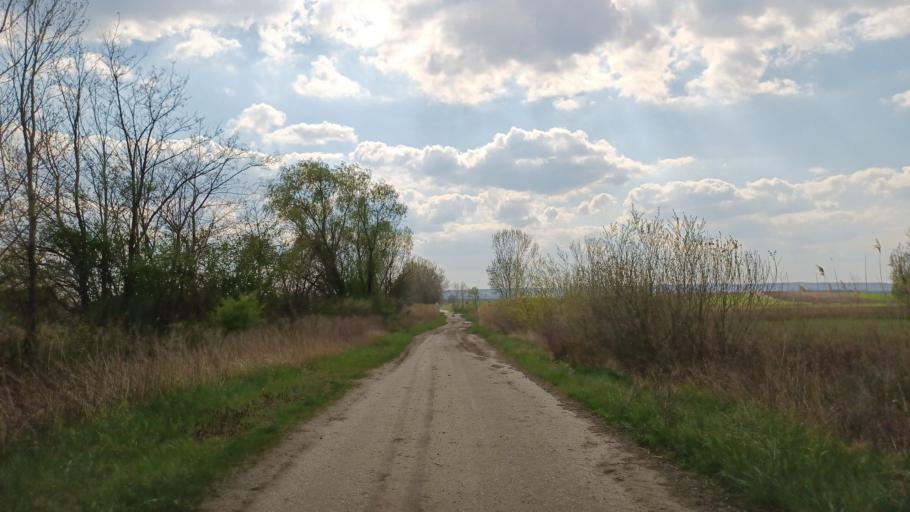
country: HU
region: Fejer
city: Cece
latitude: 46.7420
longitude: 18.6431
